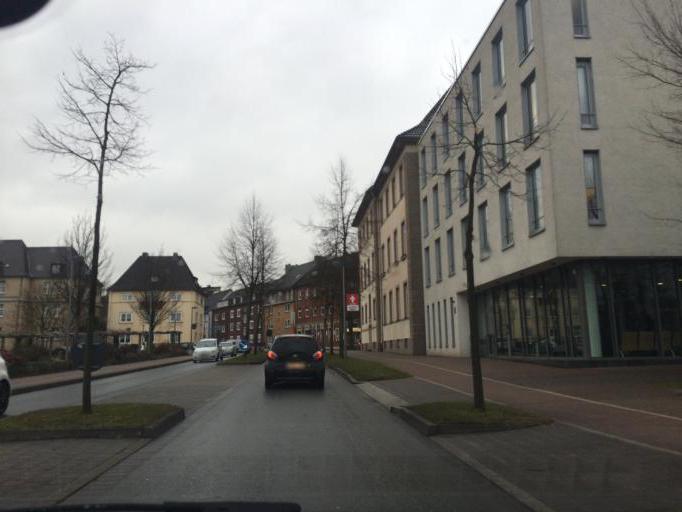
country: DE
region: North Rhine-Westphalia
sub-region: Regierungsbezirk Munster
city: Gladbeck
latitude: 51.5706
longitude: 6.9861
